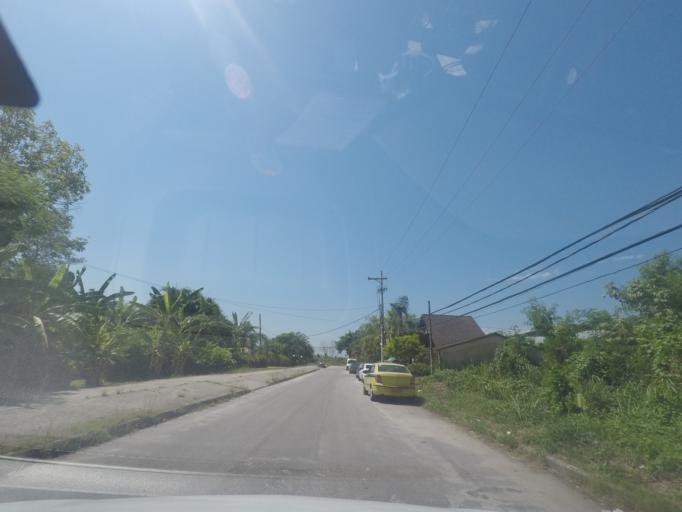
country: BR
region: Rio de Janeiro
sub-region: Nilopolis
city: Nilopolis
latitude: -22.9907
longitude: -43.4798
